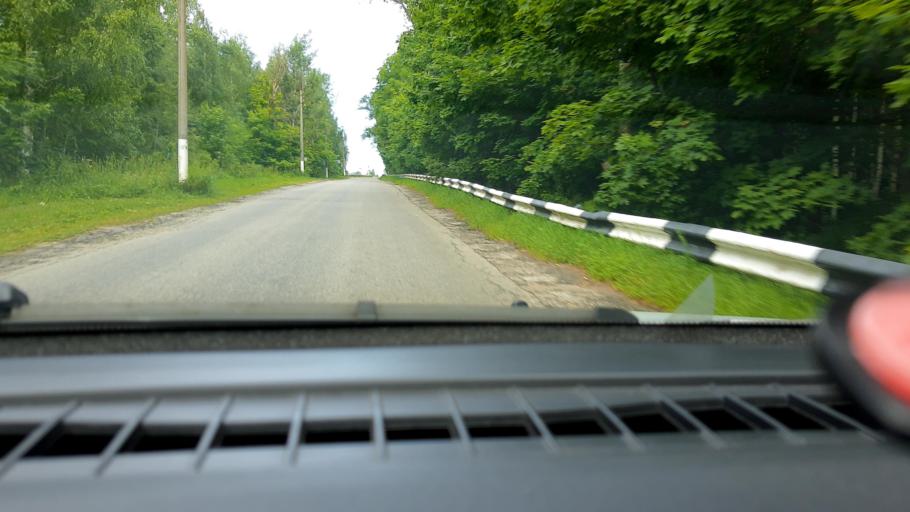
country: RU
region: Nizjnij Novgorod
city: Kstovo
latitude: 56.1468
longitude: 44.3327
